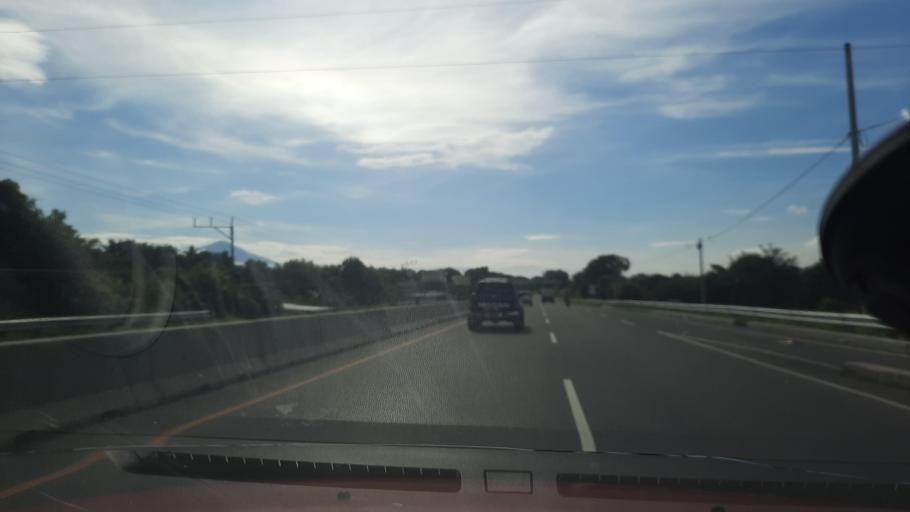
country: SV
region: La Paz
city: El Rosario
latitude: 13.4788
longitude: -89.0627
